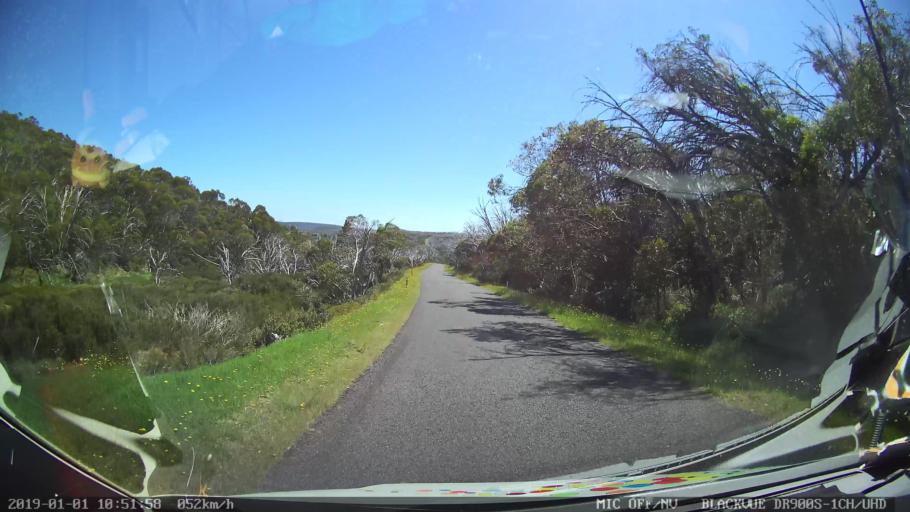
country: AU
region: New South Wales
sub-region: Snowy River
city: Jindabyne
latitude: -36.0187
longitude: 148.3766
